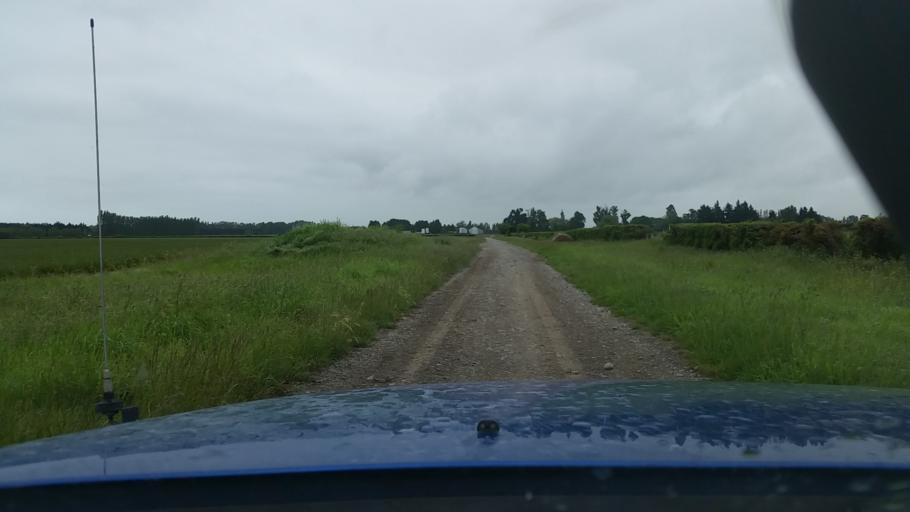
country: NZ
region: Canterbury
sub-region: Ashburton District
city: Tinwald
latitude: -43.9851
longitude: 171.7010
